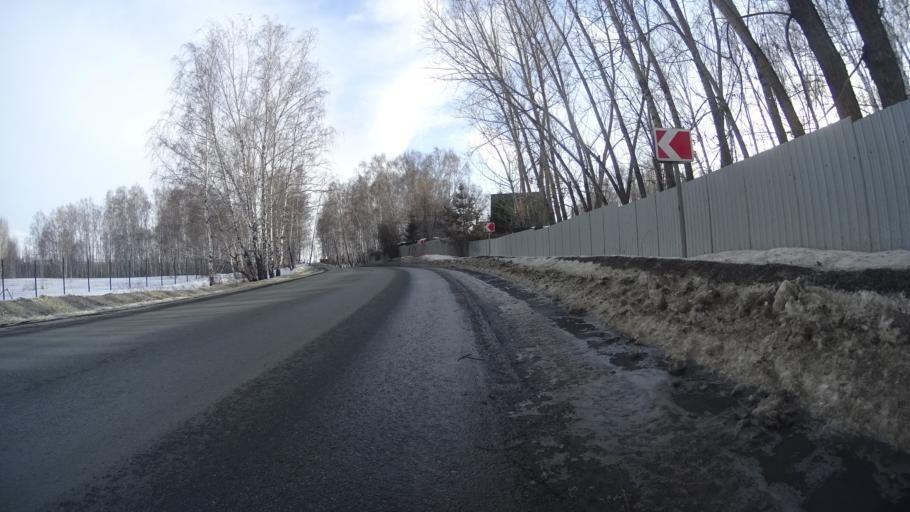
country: RU
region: Chelyabinsk
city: Sargazy
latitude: 55.1273
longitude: 61.2885
